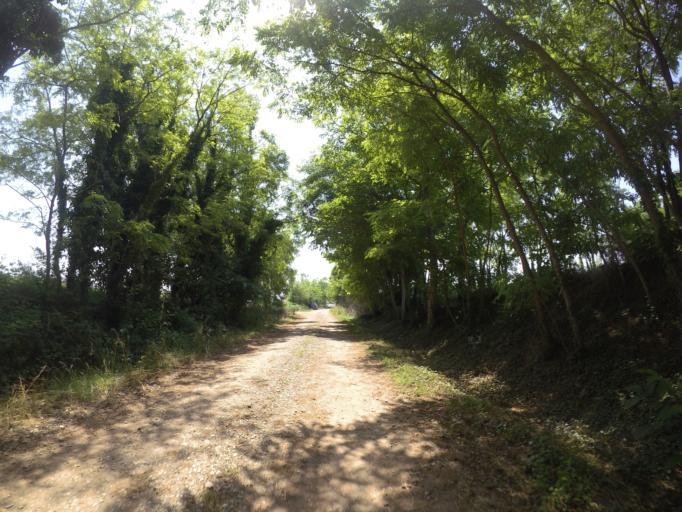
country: IT
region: Friuli Venezia Giulia
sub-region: Provincia di Udine
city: Bertiolo
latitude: 45.9612
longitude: 13.0873
